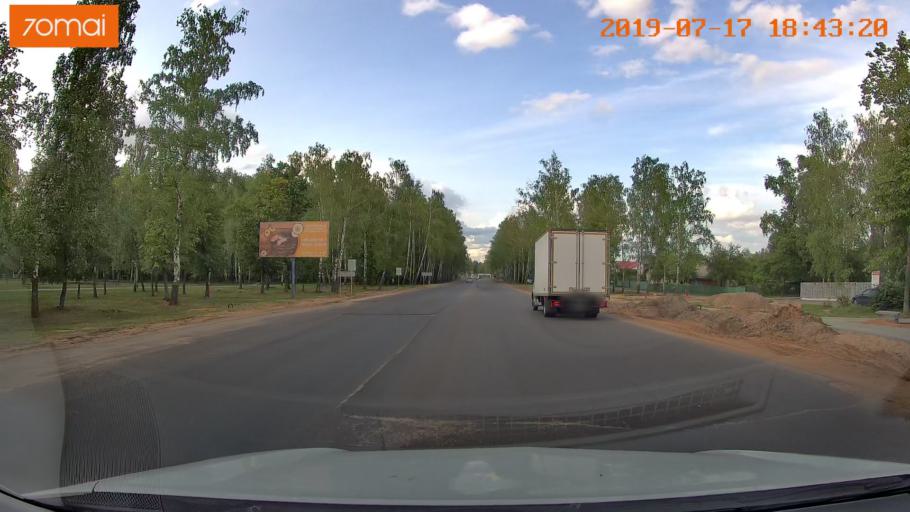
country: BY
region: Mogilev
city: Asipovichy
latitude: 53.3127
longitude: 28.6416
